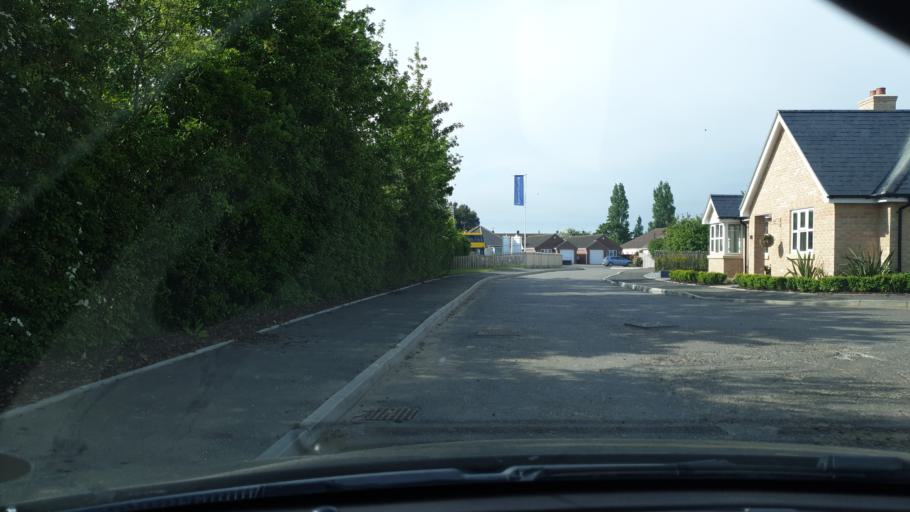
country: GB
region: England
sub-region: Essex
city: Frinton-on-Sea
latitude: 51.8428
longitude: 1.2248
